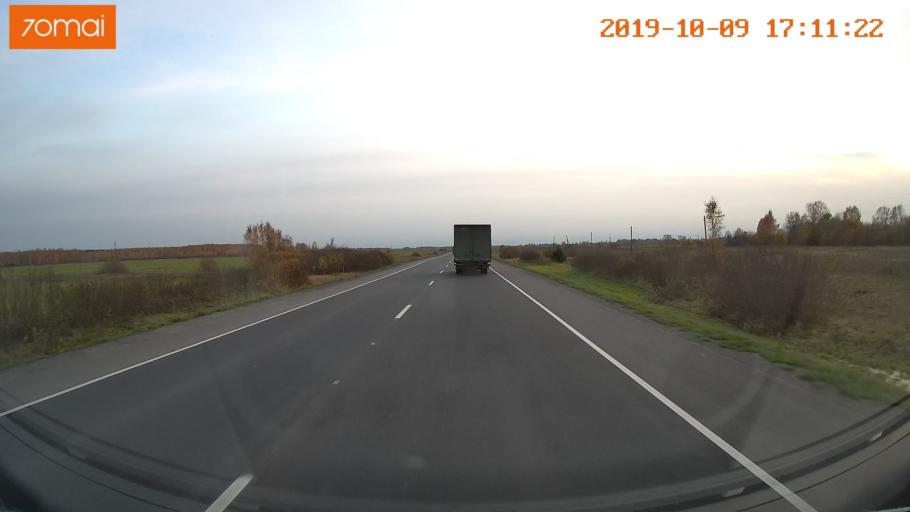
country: RU
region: Ivanovo
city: Privolzhsk
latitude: 57.3438
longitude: 41.2507
